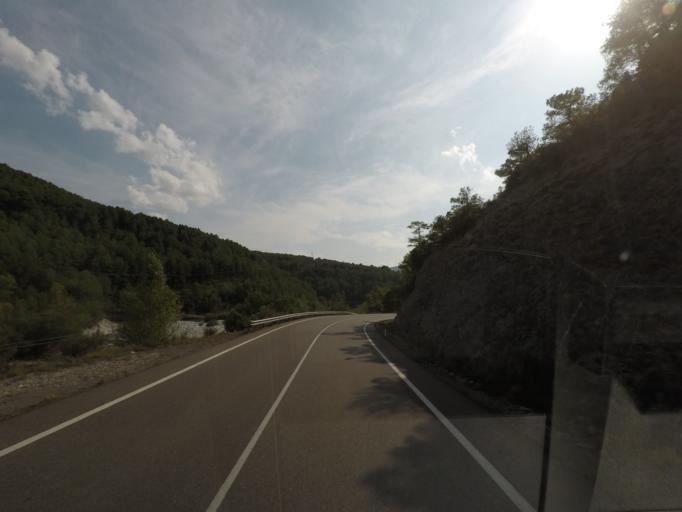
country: ES
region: Aragon
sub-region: Provincia de Huesca
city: Puertolas
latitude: 42.5331
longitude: 0.1541
